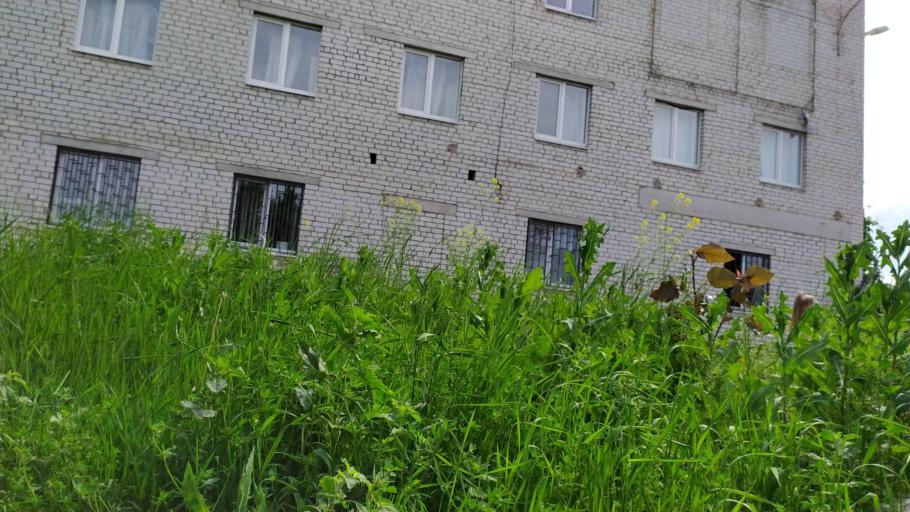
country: RU
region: Kursk
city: Kursk
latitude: 51.6641
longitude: 36.1509
